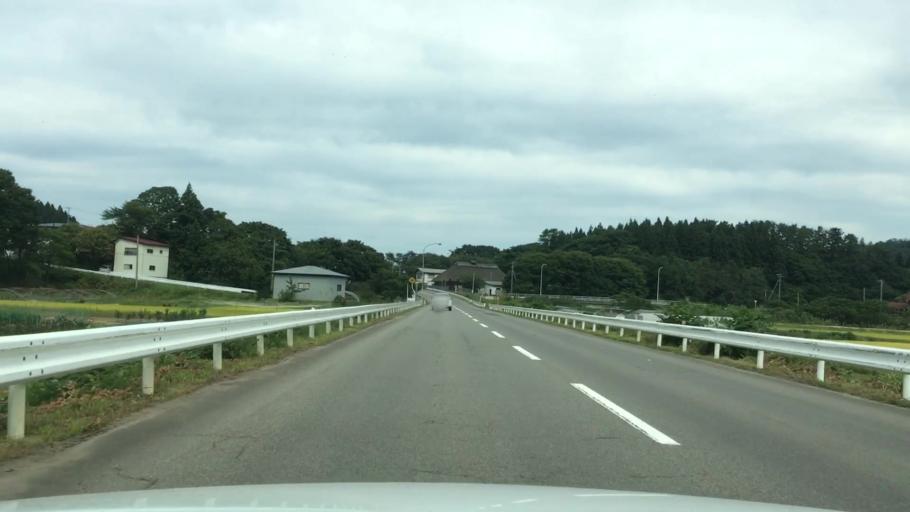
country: JP
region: Aomori
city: Shimokizukuri
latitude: 40.7553
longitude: 140.2307
